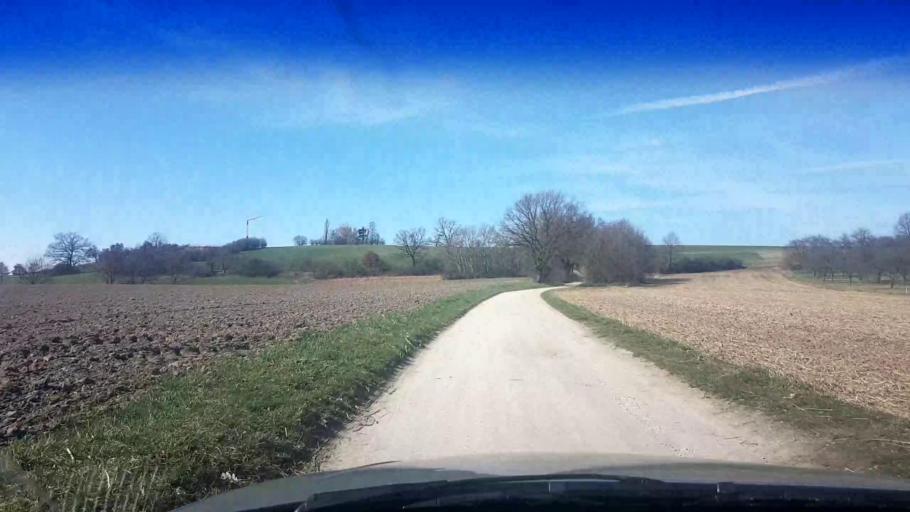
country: DE
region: Bavaria
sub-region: Upper Franconia
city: Bischberg
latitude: 49.8969
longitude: 10.8270
